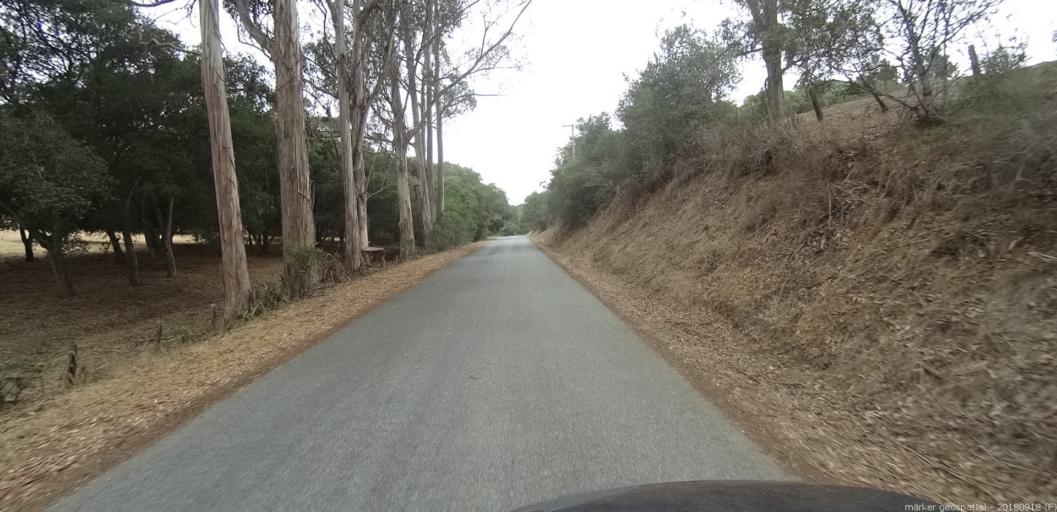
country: US
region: California
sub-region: Monterey County
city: Prunedale
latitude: 36.7814
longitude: -121.6417
